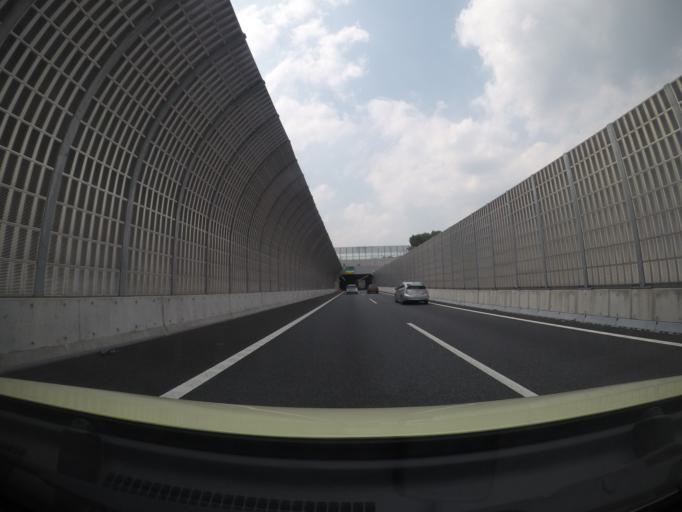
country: JP
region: Tokyo
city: Hachioji
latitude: 35.5867
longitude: 139.2897
